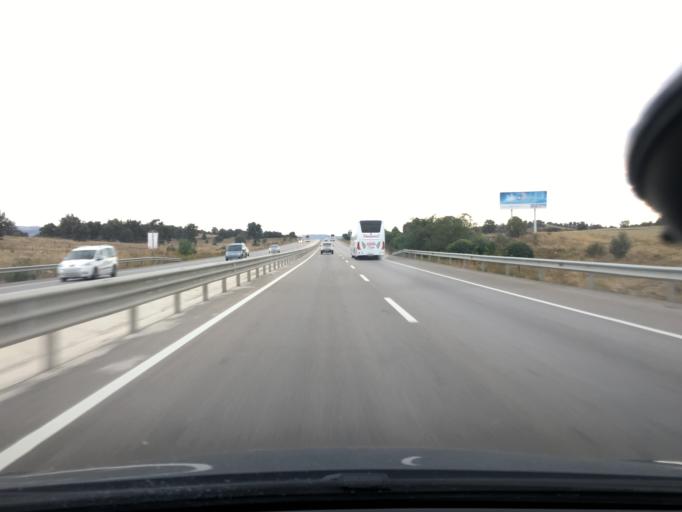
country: TR
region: Afyonkarahisar
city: Sincanli
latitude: 38.6515
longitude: 30.3168
